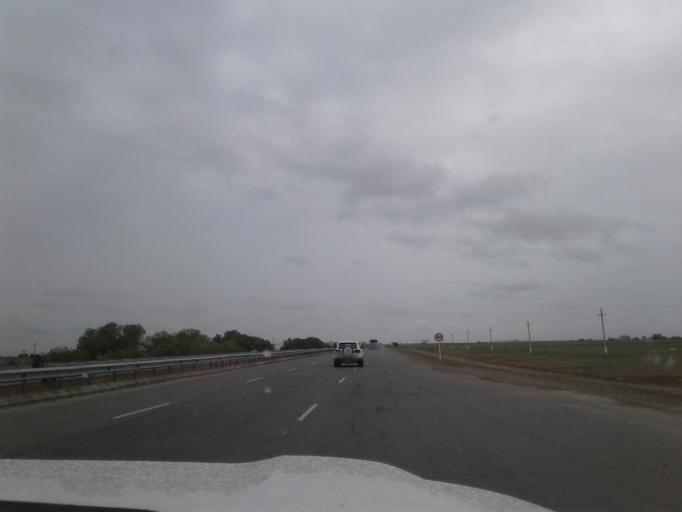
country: TM
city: Murgab
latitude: 37.6166
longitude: 62.0038
